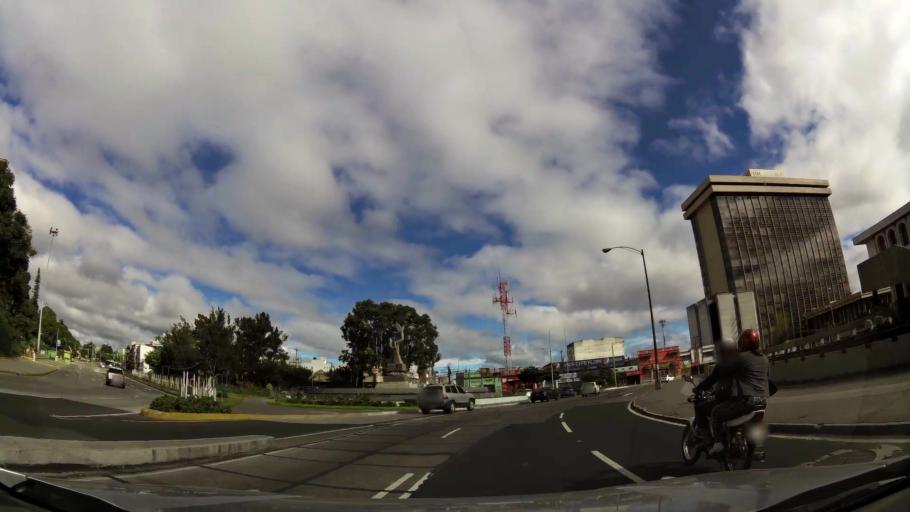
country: GT
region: Guatemala
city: Guatemala City
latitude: 14.6270
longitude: -90.5145
